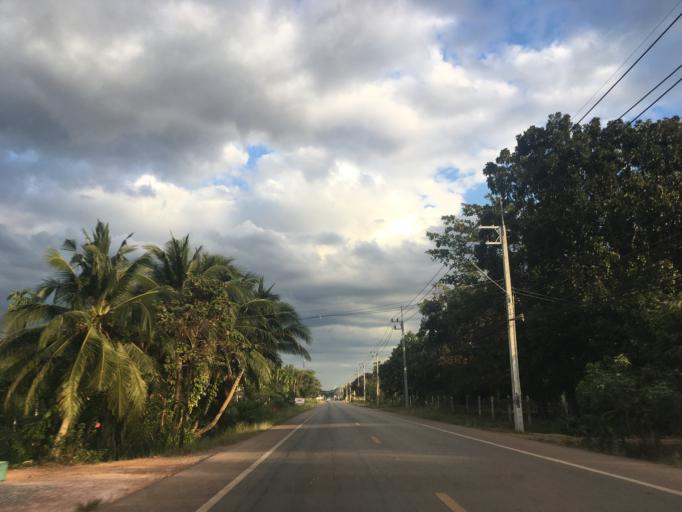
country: TH
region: Chanthaburi
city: Na Yai Am
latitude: 12.6901
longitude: 101.8132
